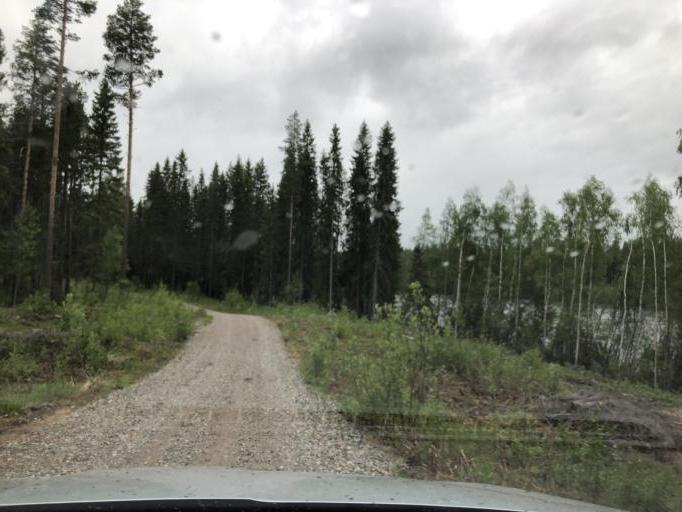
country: SE
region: Norrbotten
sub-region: Pitea Kommun
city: Roknas
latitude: 65.3995
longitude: 21.2688
